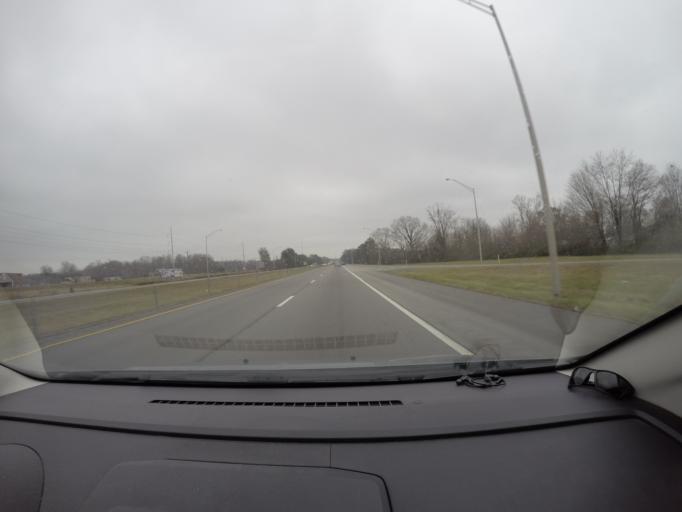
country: US
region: Tennessee
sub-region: Coffee County
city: Manchester
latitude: 35.4868
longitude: -86.0715
